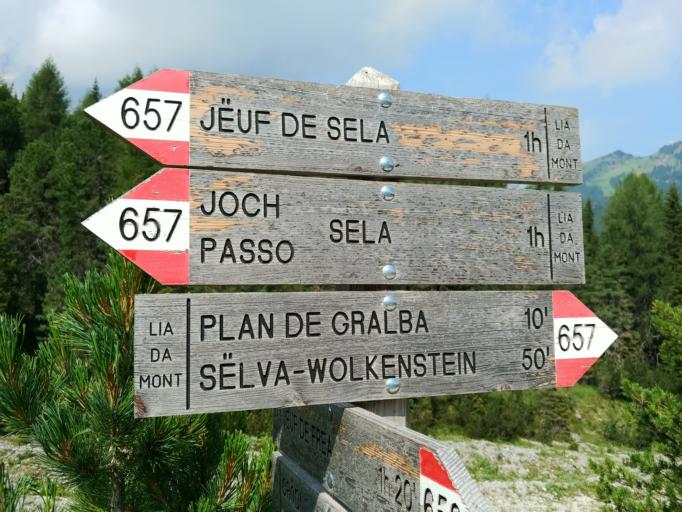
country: IT
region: Trentino-Alto Adige
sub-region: Bolzano
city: Selva
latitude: 46.5281
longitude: 11.7755
